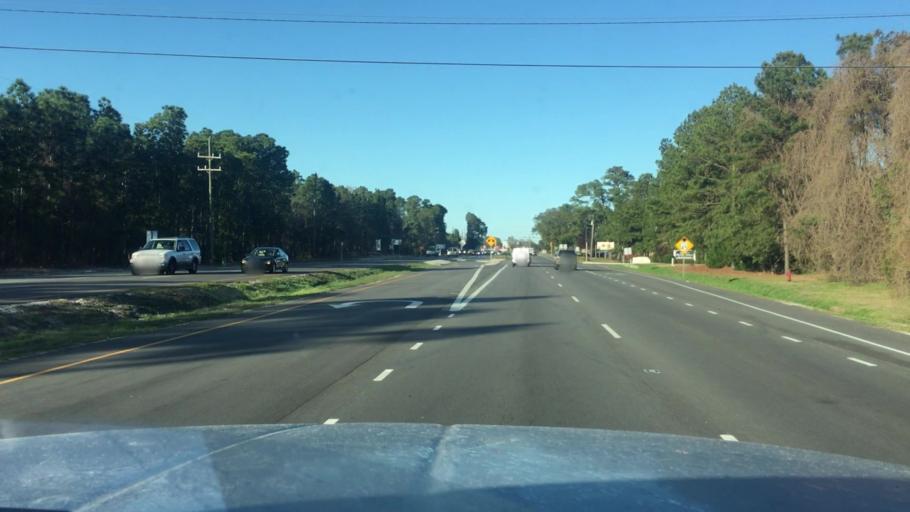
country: US
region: North Carolina
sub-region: New Hanover County
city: Myrtle Grove
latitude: 34.1287
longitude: -77.8978
